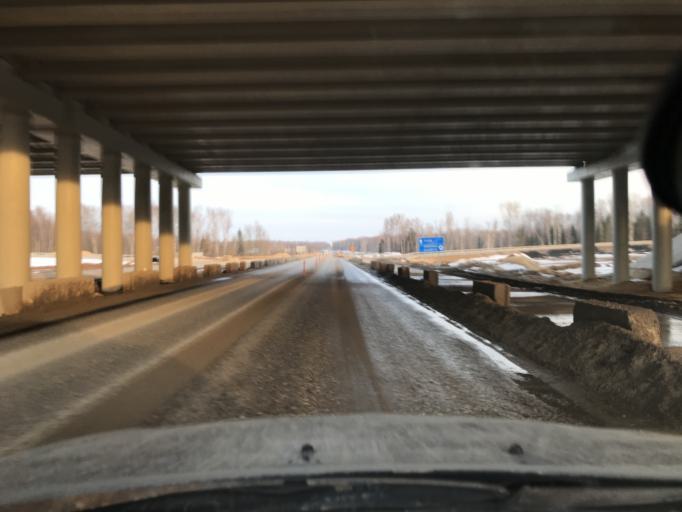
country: RU
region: Kaluga
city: Kaluga
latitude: 54.4595
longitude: 36.2724
